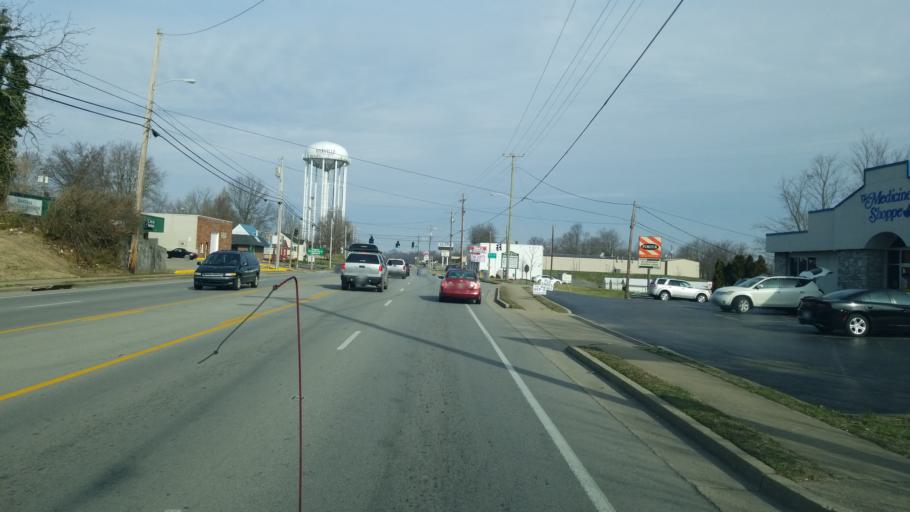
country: US
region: Kentucky
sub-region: Boyle County
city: Danville
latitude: 37.6304
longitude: -84.7748
